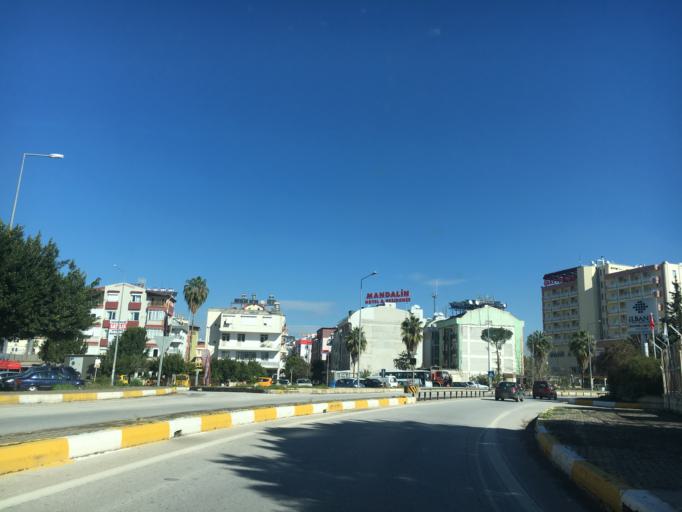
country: TR
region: Antalya
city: Antalya
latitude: 36.9017
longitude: 30.6628
